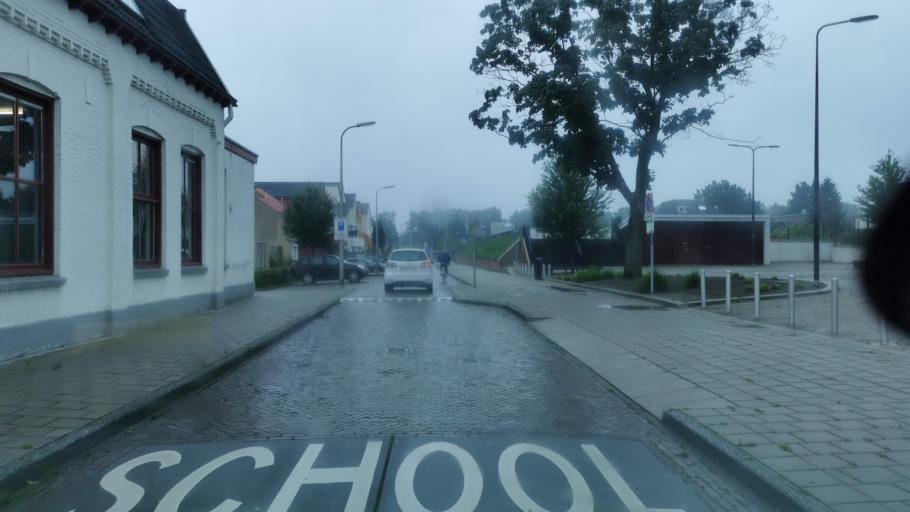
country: NL
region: Overijssel
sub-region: Gemeente Enschede
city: Enschede
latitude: 52.2210
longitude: 6.9035
